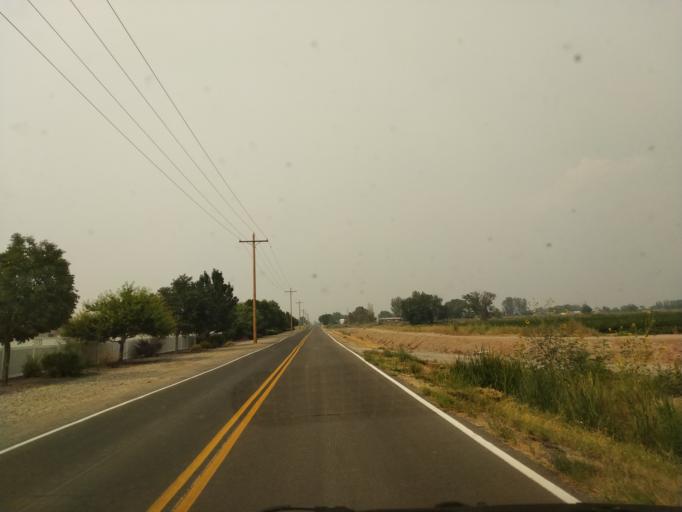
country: US
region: Colorado
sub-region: Mesa County
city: Fruitvale
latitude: 39.0314
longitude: -108.4967
